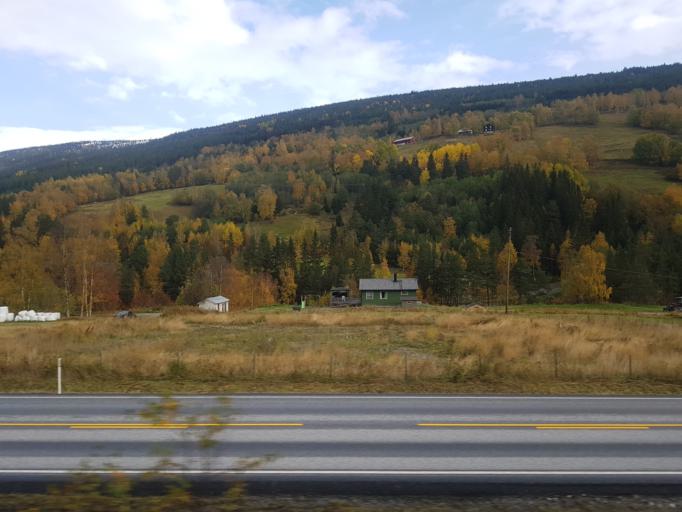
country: NO
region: Oppland
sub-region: Dovre
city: Dovre
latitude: 61.9288
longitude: 9.3215
